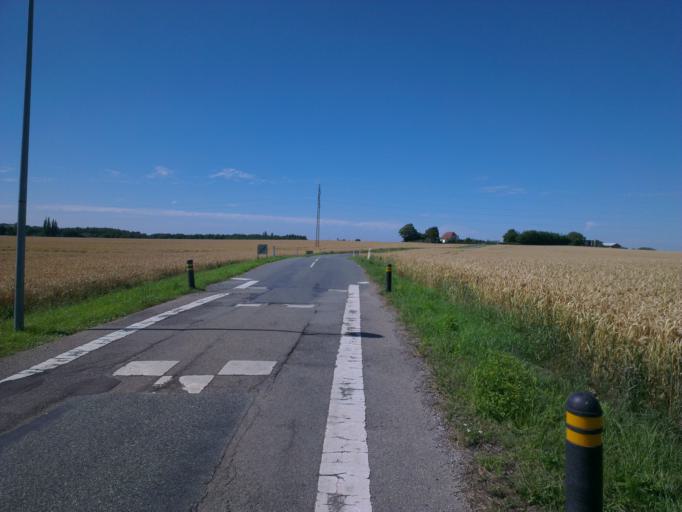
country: DK
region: Capital Region
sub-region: Frederikssund Kommune
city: Frederikssund
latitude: 55.8642
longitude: 12.0949
